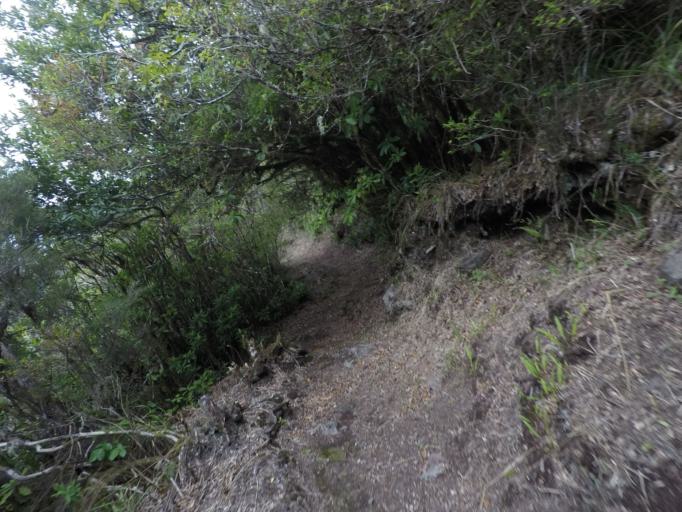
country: PT
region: Madeira
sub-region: Camara de Lobos
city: Curral das Freiras
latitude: 32.7650
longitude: -16.9754
